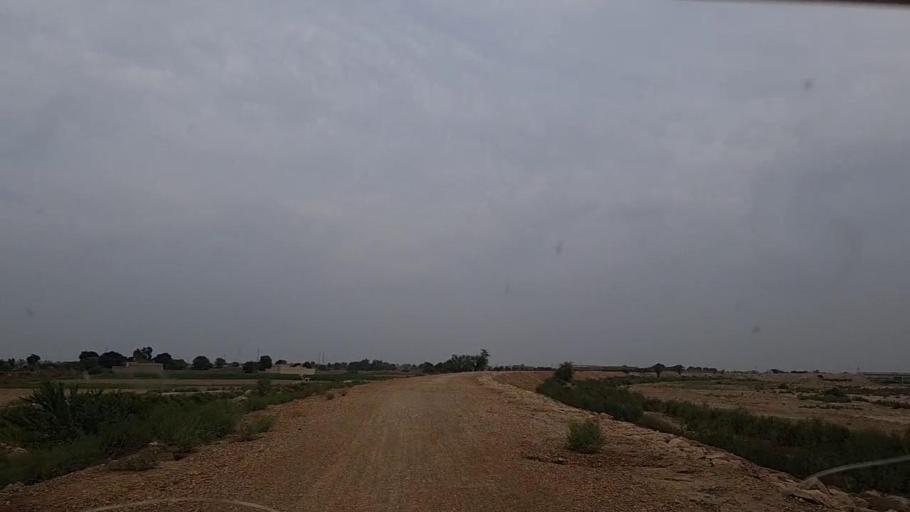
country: PK
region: Sindh
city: Johi
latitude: 26.7025
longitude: 67.5972
